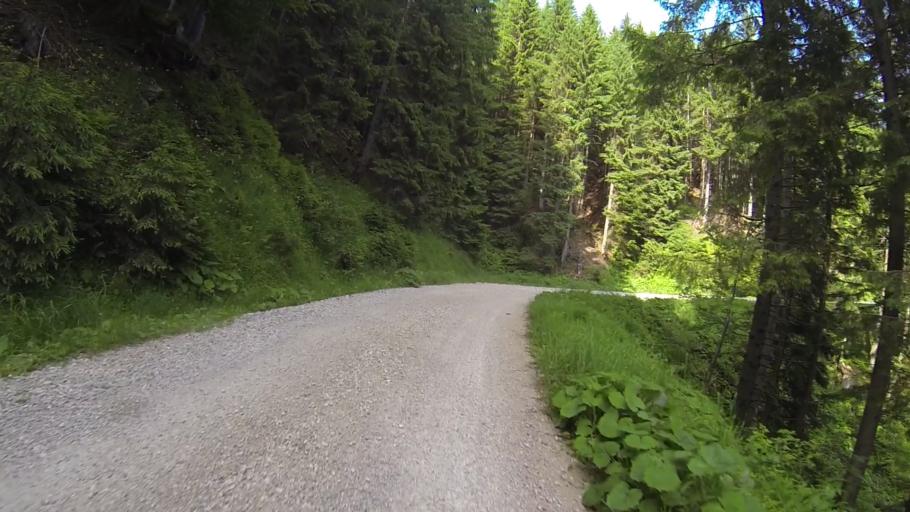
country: DE
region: Bavaria
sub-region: Swabia
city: Nesselwang
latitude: 47.5867
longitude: 10.4962
